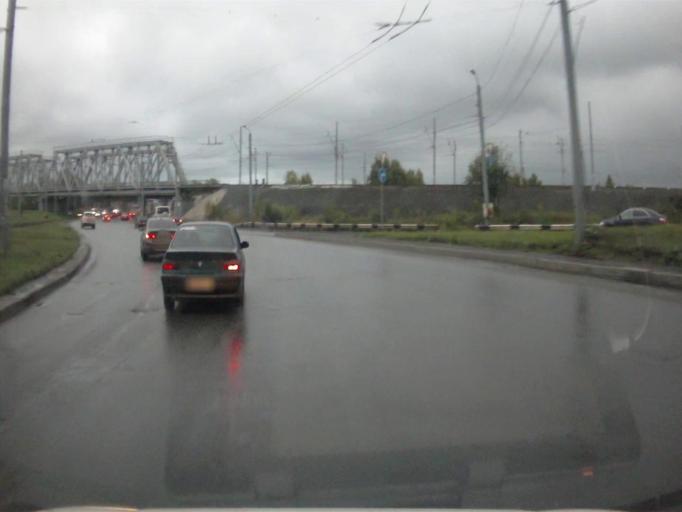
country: RU
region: Chelyabinsk
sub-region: Gorod Chelyabinsk
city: Chelyabinsk
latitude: 55.1561
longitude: 61.4432
